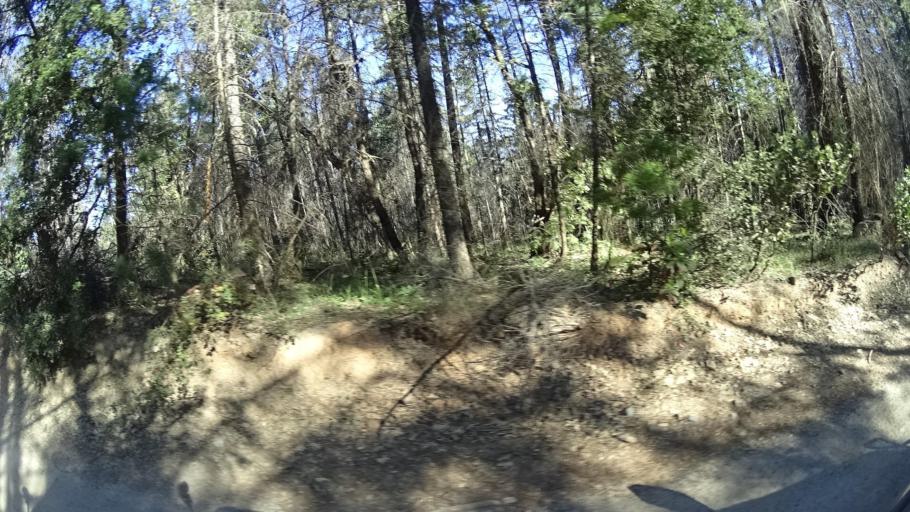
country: US
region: California
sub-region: Lake County
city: Upper Lake
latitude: 39.3818
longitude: -122.9856
